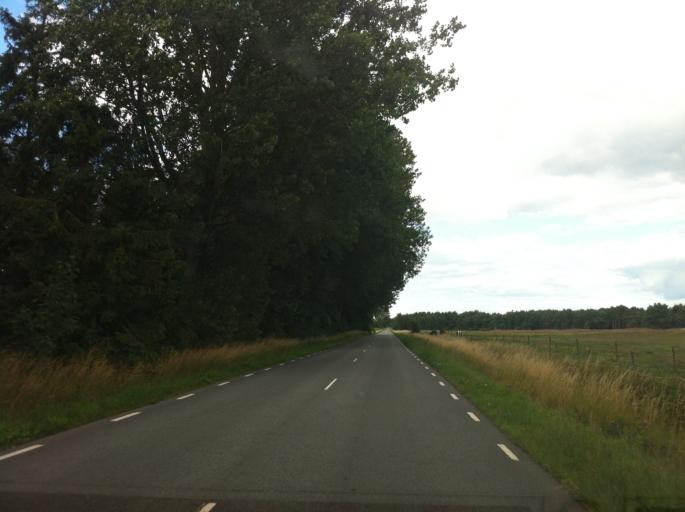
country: SE
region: Skane
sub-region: Simrishamns Kommun
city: Simrishamn
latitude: 55.4135
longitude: 14.2018
